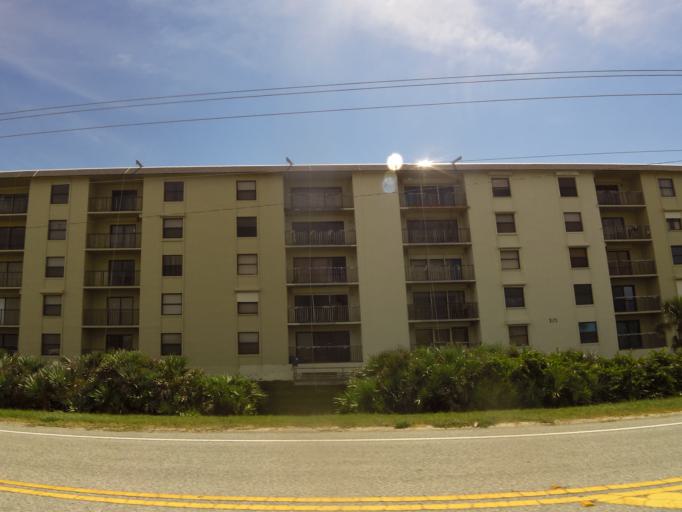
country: US
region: Florida
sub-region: Volusia County
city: Ormond-by-the-Sea
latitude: 29.3725
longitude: -81.0778
